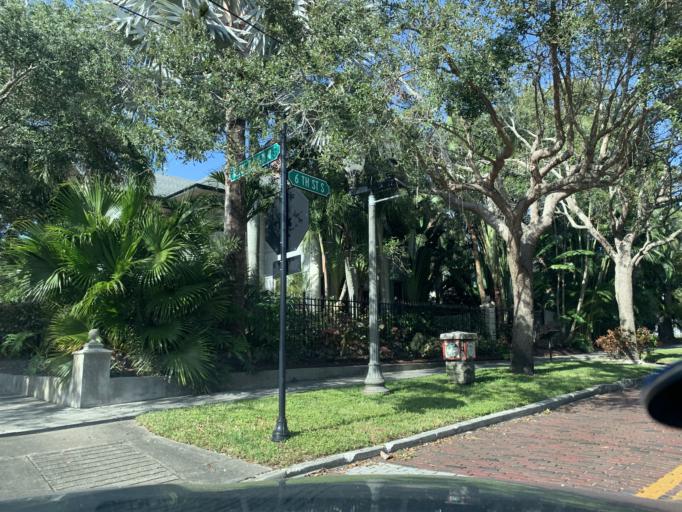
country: US
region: Florida
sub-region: Pinellas County
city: Saint Petersburg
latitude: 27.7595
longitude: -82.6420
